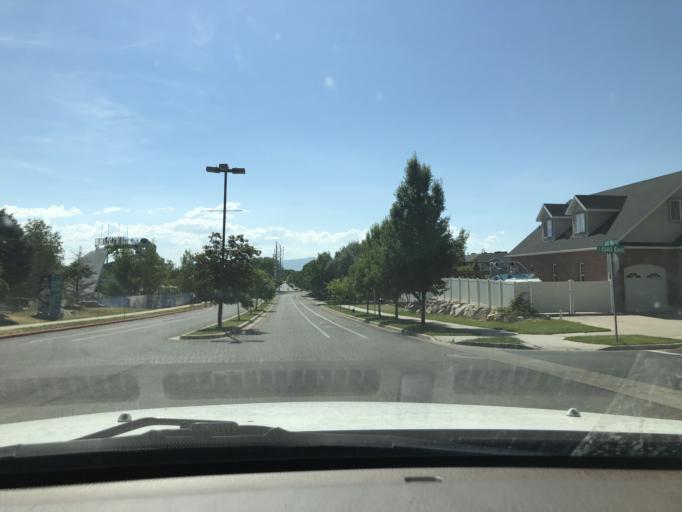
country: US
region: Utah
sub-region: Utah County
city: Provo
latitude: 40.2374
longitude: -111.6351
